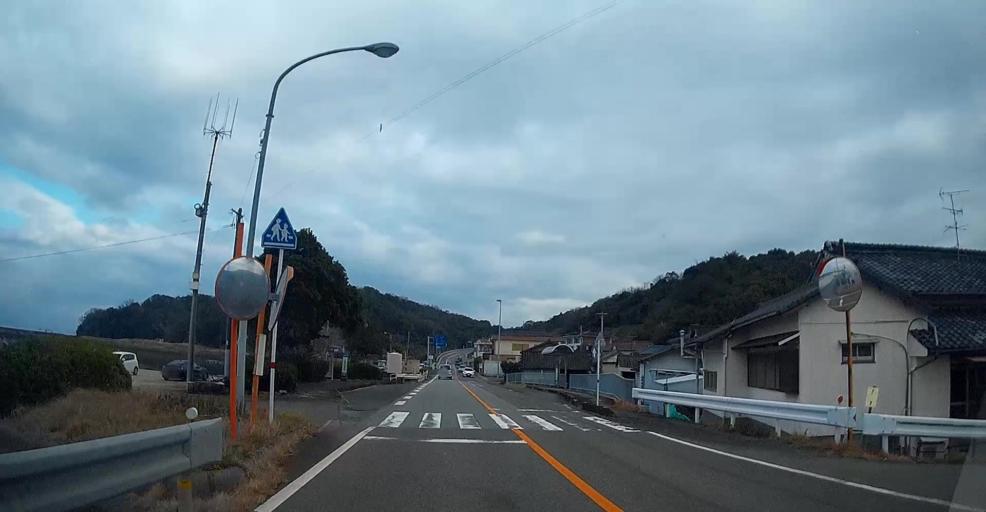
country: JP
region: Kumamoto
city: Hondo
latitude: 32.4914
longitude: 130.2932
